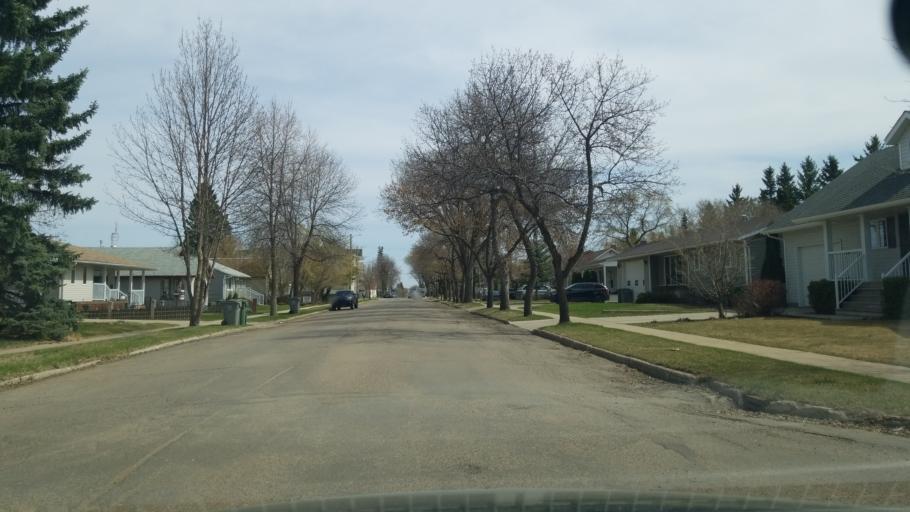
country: CA
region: Saskatchewan
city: Lloydminster
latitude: 53.2816
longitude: -110.0130
